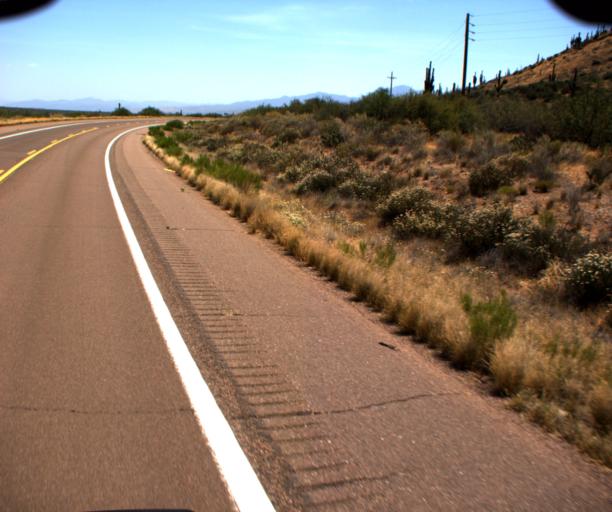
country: US
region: Arizona
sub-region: Gila County
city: Tonto Basin
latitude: 33.9092
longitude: -111.3107
